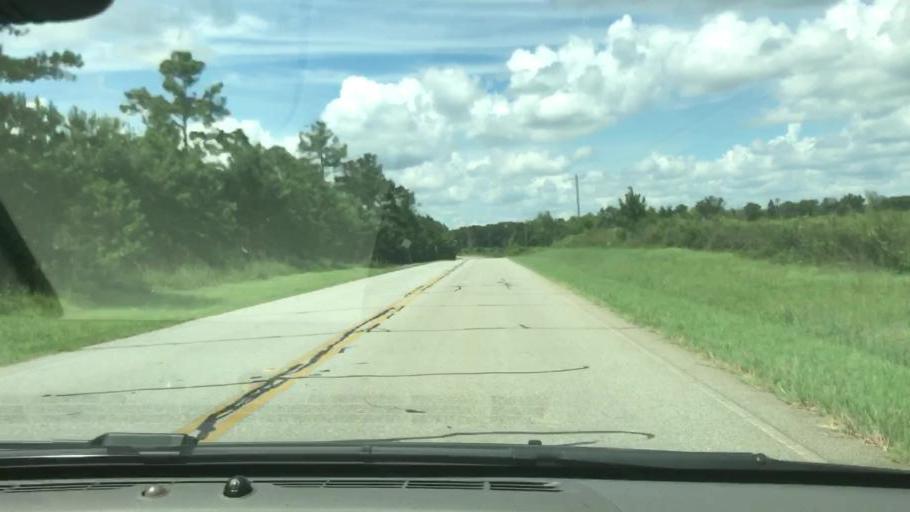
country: US
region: Georgia
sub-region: Stewart County
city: Lumpkin
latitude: 32.1321
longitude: -84.9900
